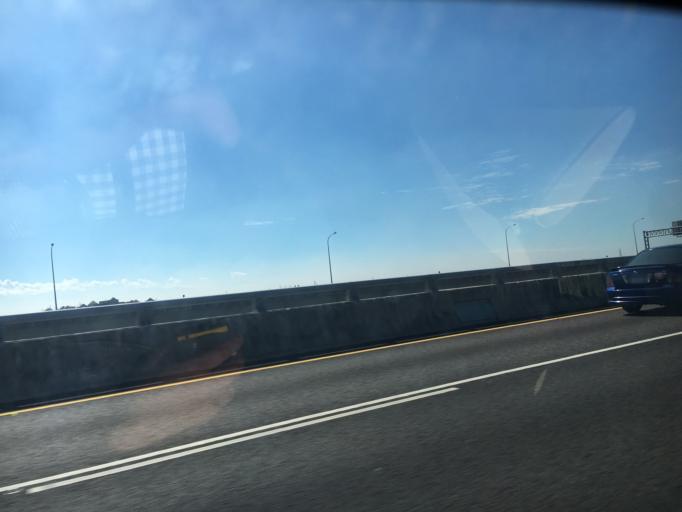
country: TW
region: Taiwan
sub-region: Taoyuan
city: Taoyuan
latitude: 25.0655
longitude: 121.3571
